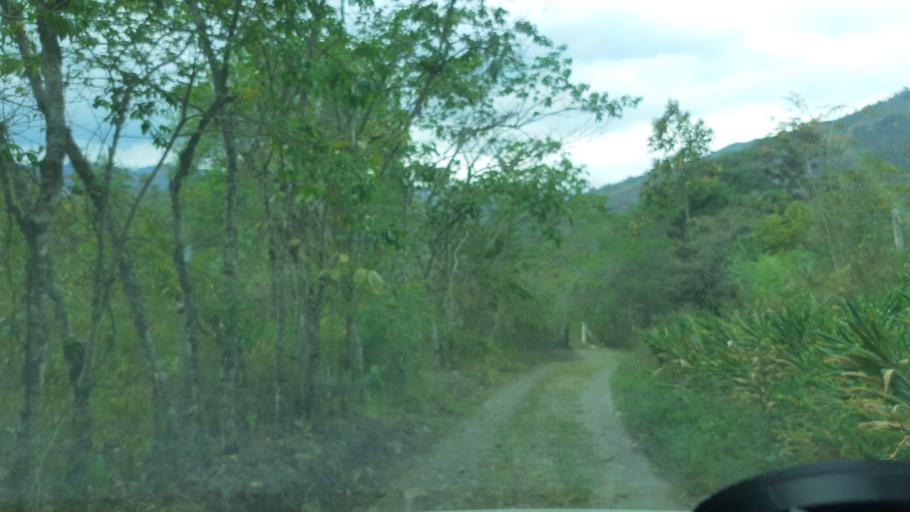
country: CO
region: Boyaca
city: Garagoa
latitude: 5.0090
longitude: -73.3653
